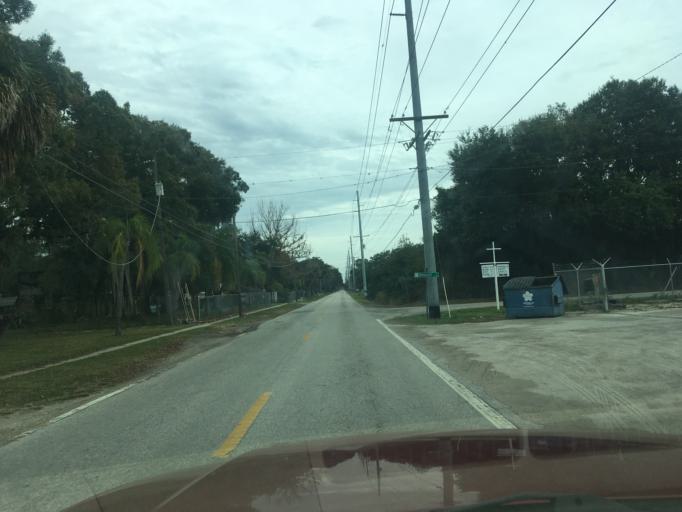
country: US
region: Florida
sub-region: Hillsborough County
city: Gibsonton
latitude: 27.8461
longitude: -82.3779
